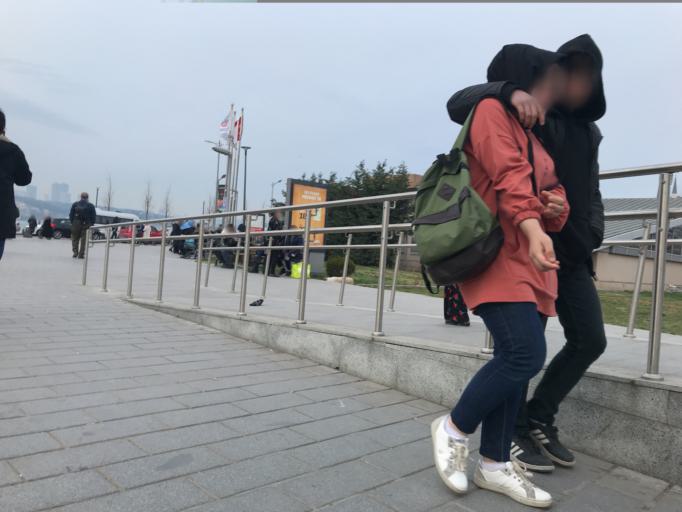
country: TR
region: Istanbul
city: UEskuedar
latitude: 41.0256
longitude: 29.0130
